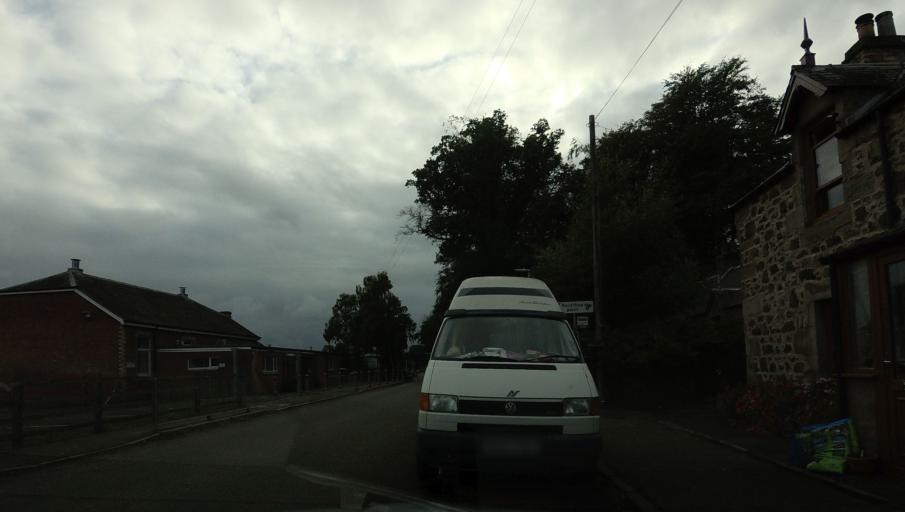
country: GB
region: Scotland
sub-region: Perth and Kinross
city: Abernethy
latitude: 56.3796
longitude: -3.3031
